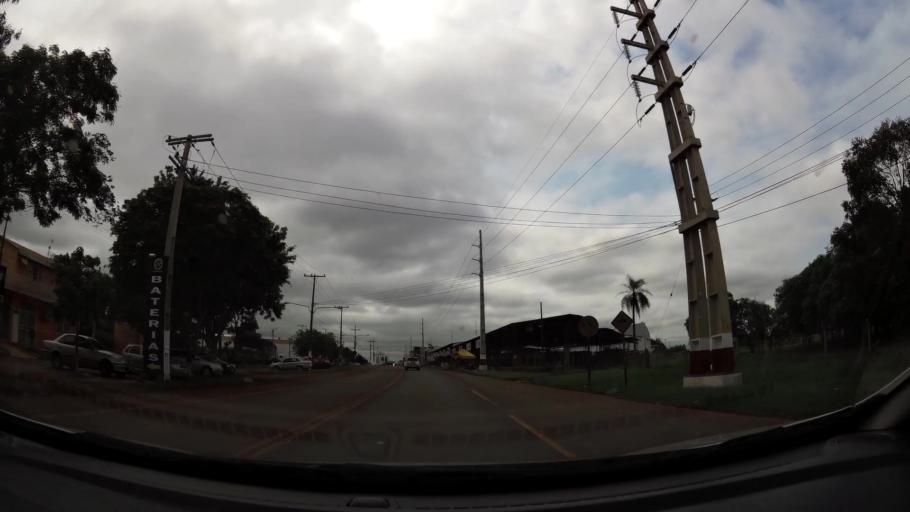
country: PY
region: Alto Parana
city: Ciudad del Este
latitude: -25.3923
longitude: -54.6372
